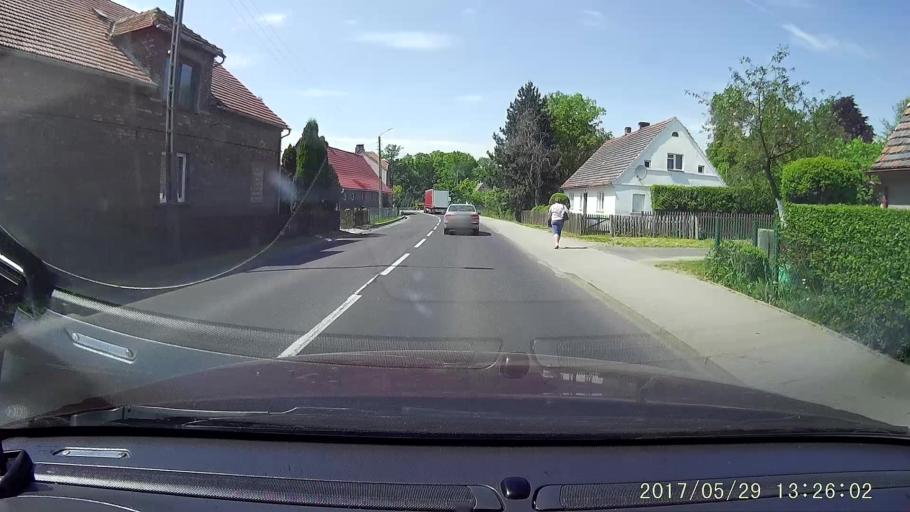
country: PL
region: Lower Silesian Voivodeship
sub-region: Powiat lubanski
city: Olszyna
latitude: 51.0434
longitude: 15.3780
